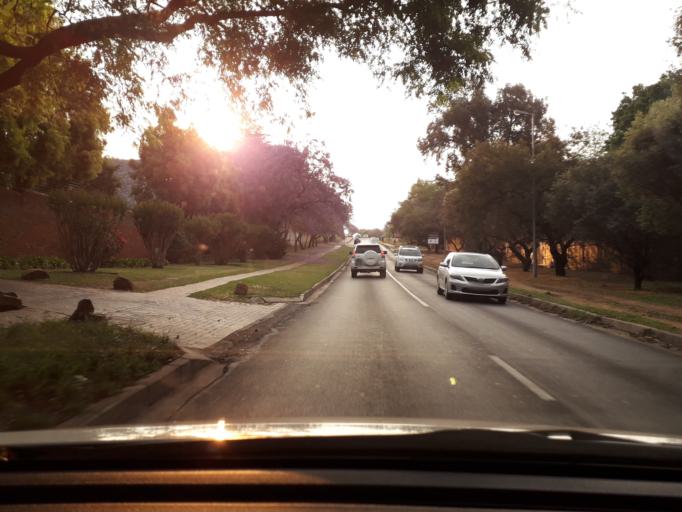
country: ZA
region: Gauteng
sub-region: City of Johannesburg Metropolitan Municipality
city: Diepsloot
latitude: -26.0474
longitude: 28.0279
